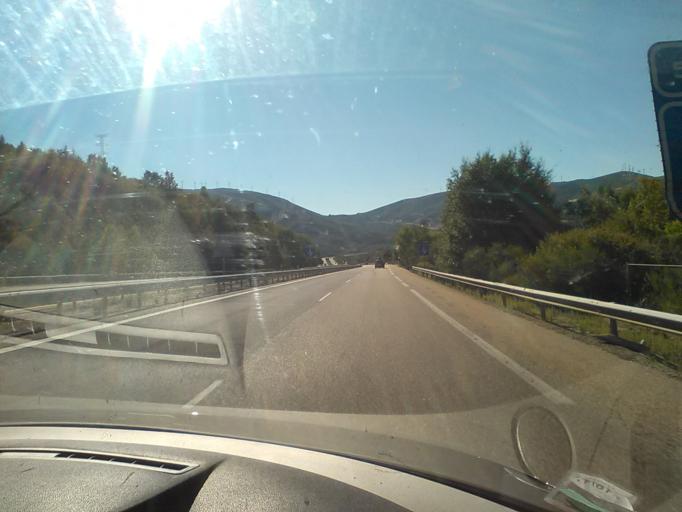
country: ES
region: Castille and Leon
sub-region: Provincia de Zamora
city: Lubian
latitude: 42.0283
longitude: -6.8997
